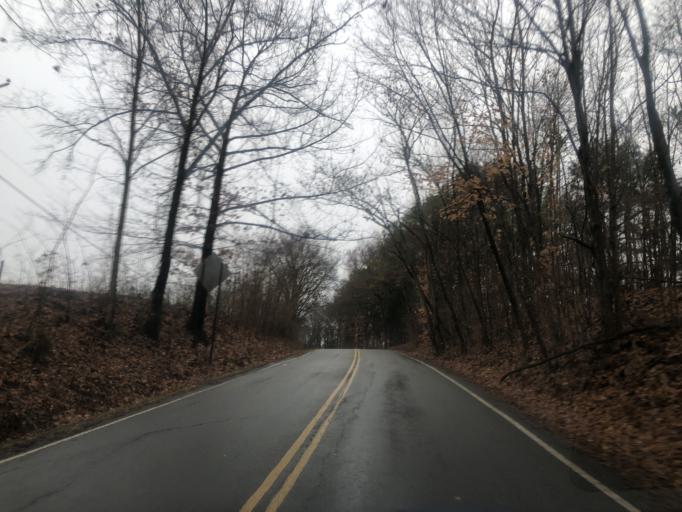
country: US
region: Tennessee
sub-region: Cheatham County
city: Pegram
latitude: 36.0825
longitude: -86.9555
